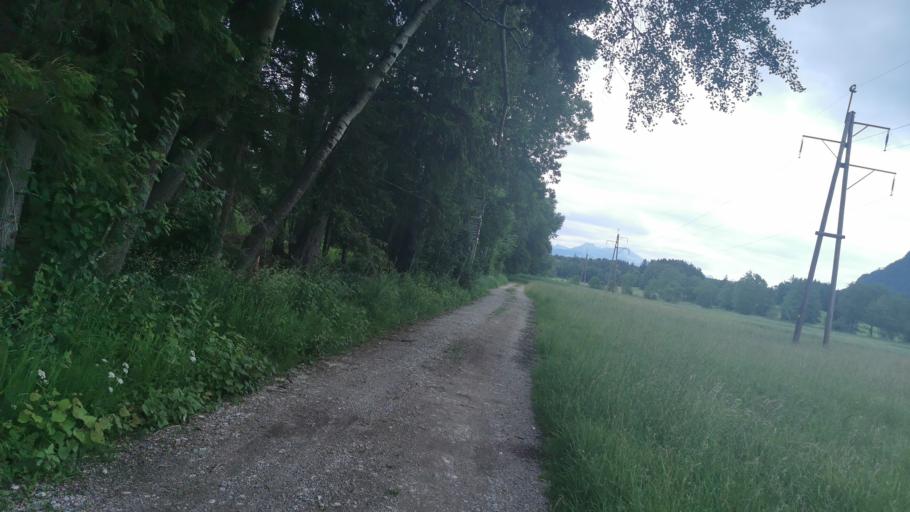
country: DE
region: Bavaria
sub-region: Upper Bavaria
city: Ainring
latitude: 47.7671
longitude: 12.9794
